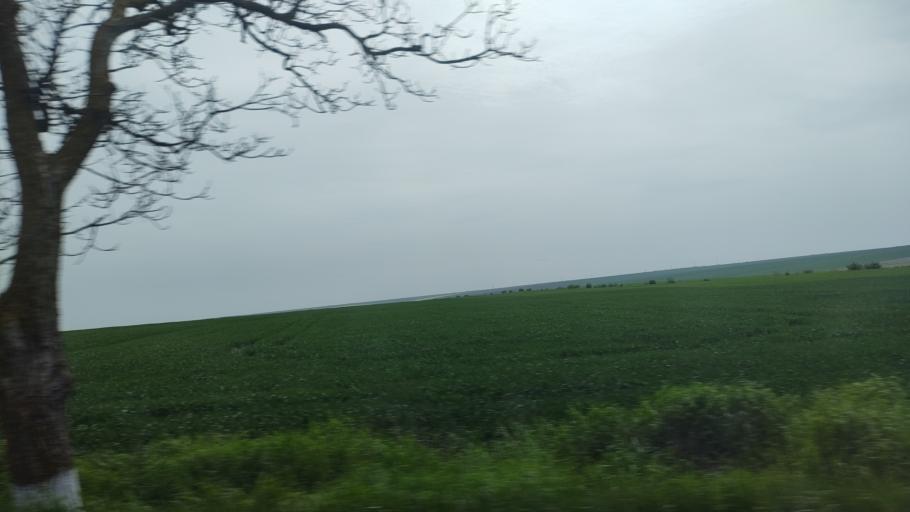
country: RO
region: Constanta
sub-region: Comuna Ciocarlia
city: Ciocarlia de Sus
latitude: 44.1300
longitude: 28.3433
